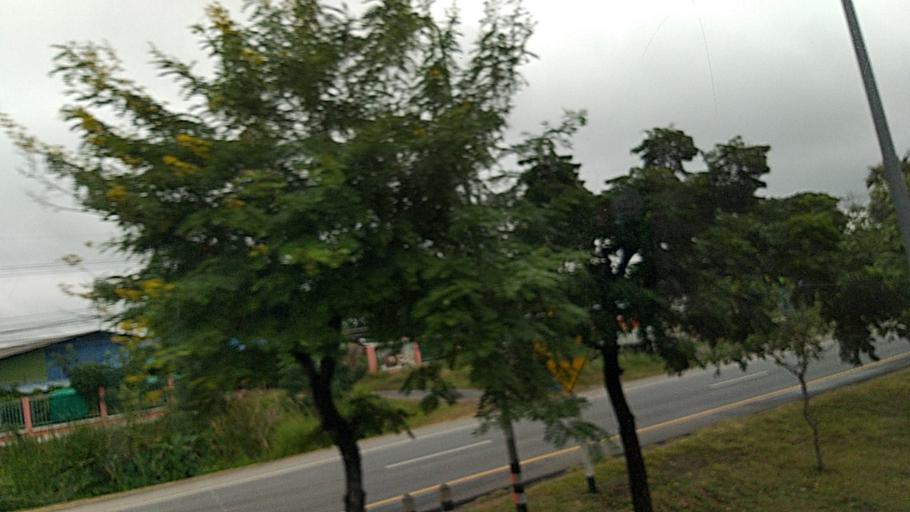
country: TH
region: Nakhon Ratchasima
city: Nakhon Ratchasima
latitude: 15.0478
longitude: 102.1538
